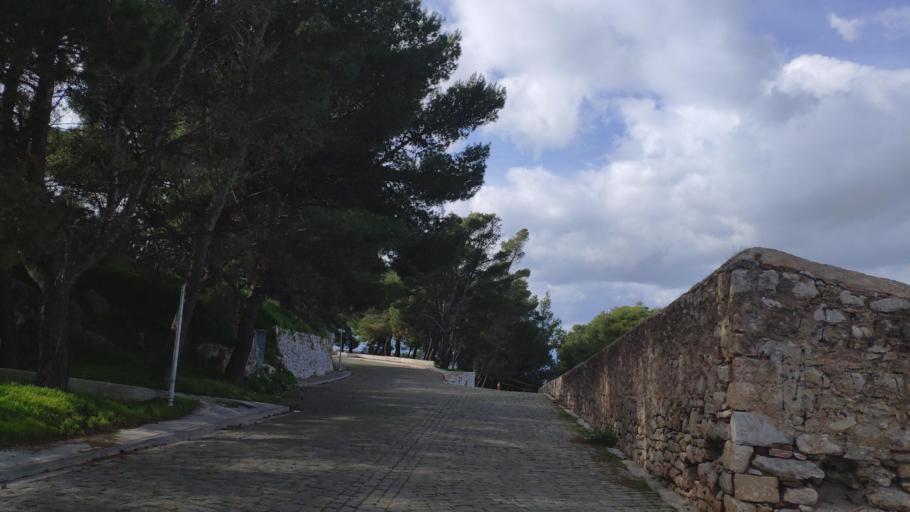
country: GR
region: Peloponnese
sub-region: Nomos Argolidos
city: Nafplio
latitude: 37.5645
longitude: 22.7960
